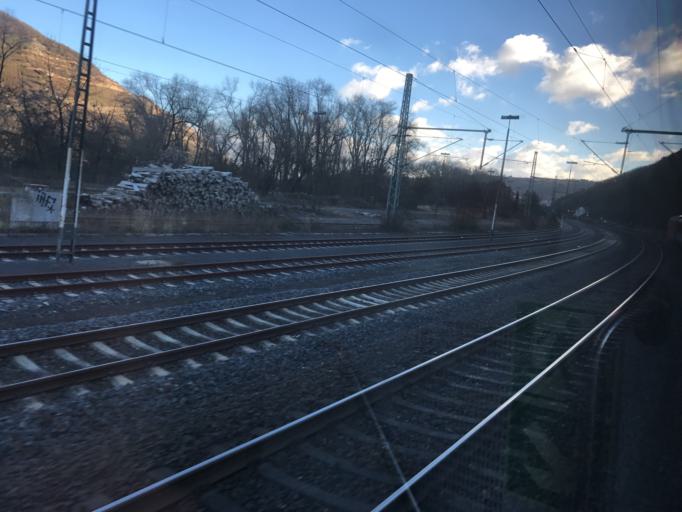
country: DE
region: Rheinland-Pfalz
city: Weiler
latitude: 49.9746
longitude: 7.8660
